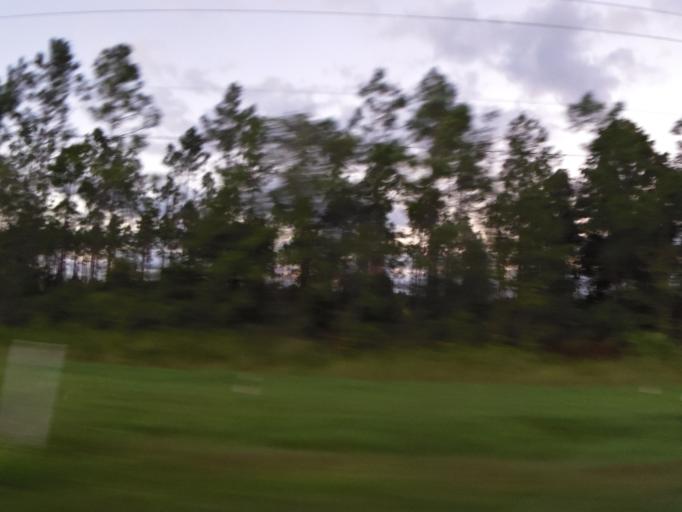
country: US
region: Florida
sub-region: Saint Johns County
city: Palm Valley
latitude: 30.0832
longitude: -81.4634
